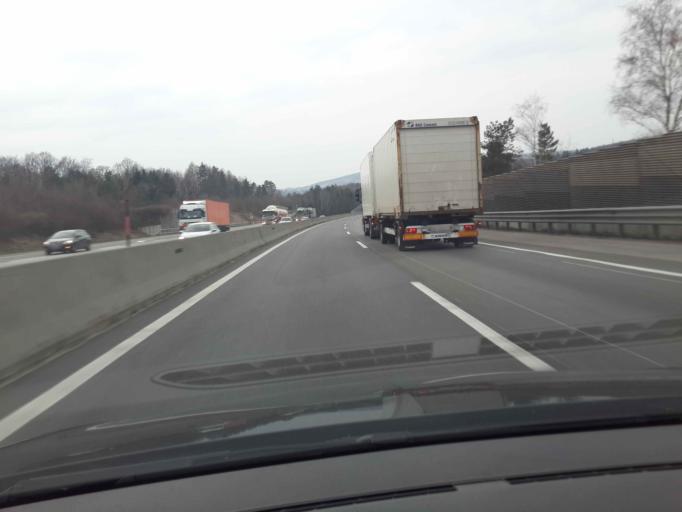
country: AT
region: Lower Austria
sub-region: Politischer Bezirk Sankt Polten
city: Eichgraben
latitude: 48.1511
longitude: 15.9739
